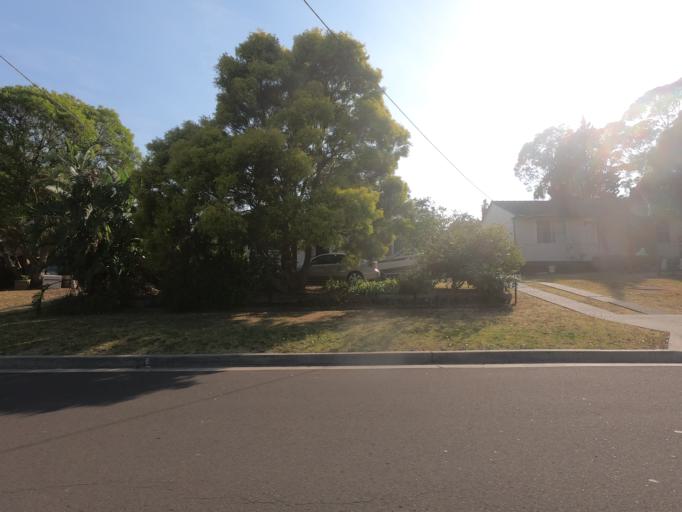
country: AU
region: New South Wales
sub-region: Wollongong
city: Berkeley
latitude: -34.4737
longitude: 150.8439
